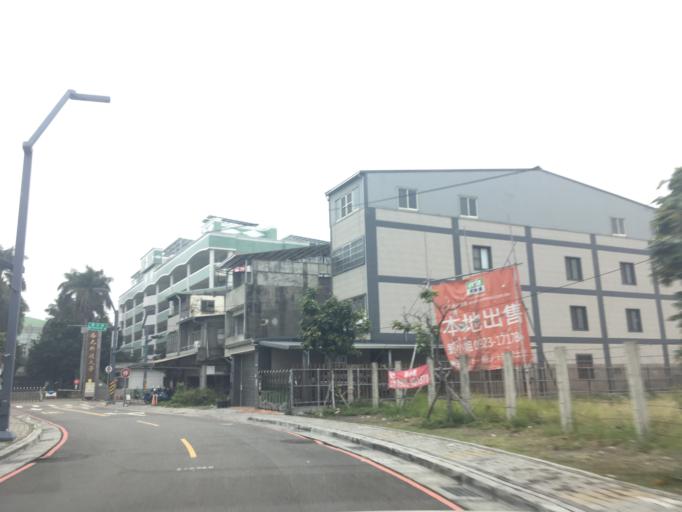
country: TW
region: Taiwan
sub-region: Taichung City
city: Taichung
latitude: 24.1896
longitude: 120.6425
